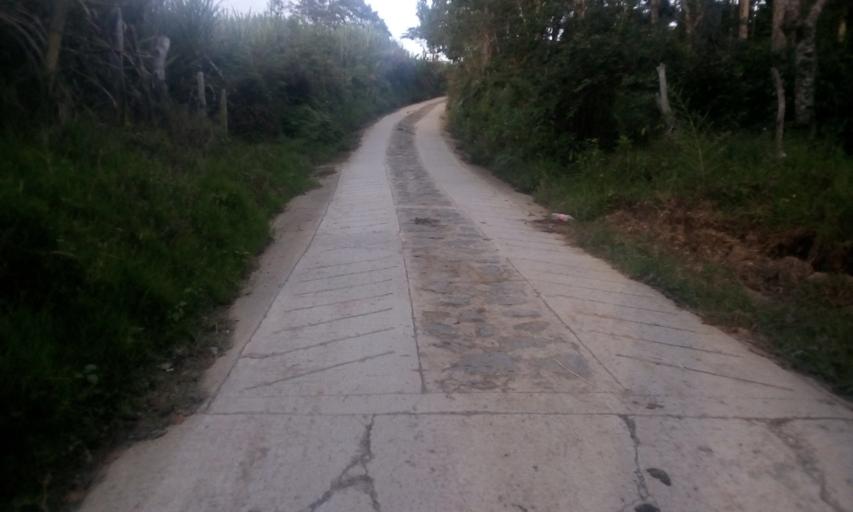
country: CO
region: Boyaca
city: Santana
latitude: 6.0044
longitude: -73.5061
